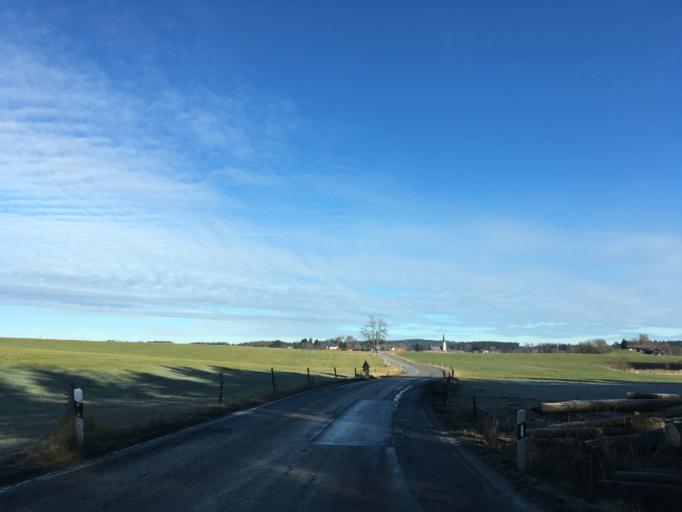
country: DE
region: Bavaria
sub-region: Upper Bavaria
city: Babensham
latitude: 48.0733
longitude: 12.2636
